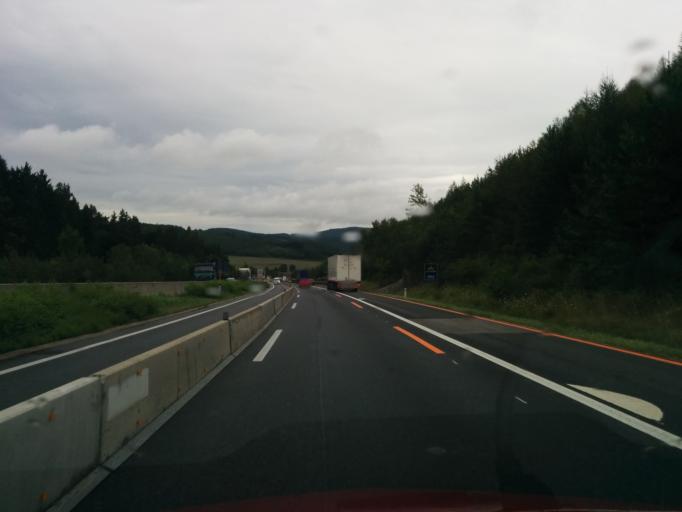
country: AT
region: Lower Austria
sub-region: Politischer Bezirk Baden
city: Heiligenkreuz
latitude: 48.0594
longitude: 16.1123
